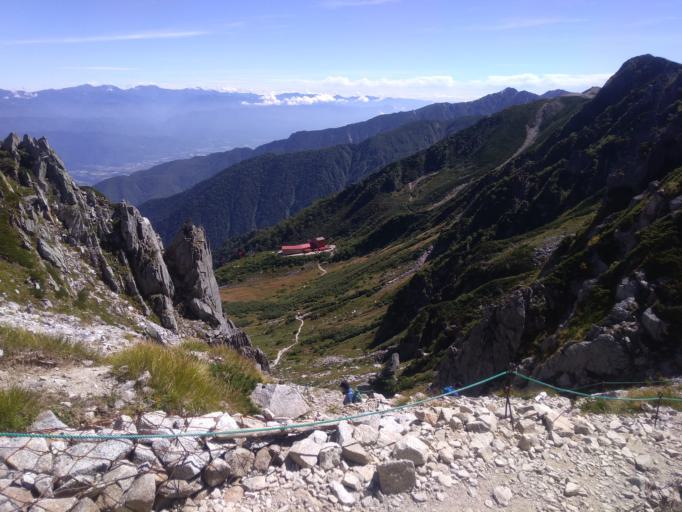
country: JP
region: Nagano
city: Ina
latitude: 35.7831
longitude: 137.8104
